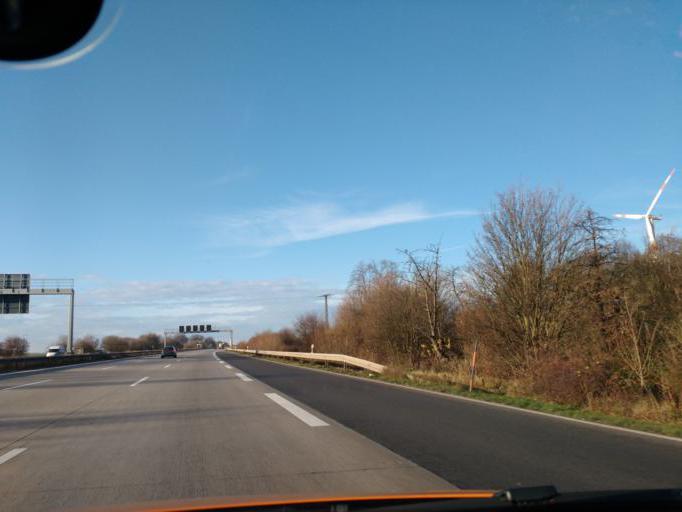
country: DE
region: Saxony-Anhalt
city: Eichenbarleben
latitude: 52.1872
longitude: 11.3557
